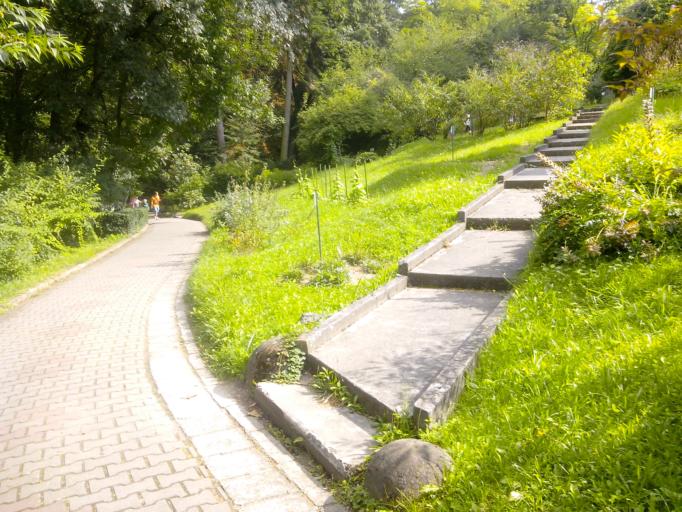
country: RO
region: Cluj
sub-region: Municipiul Cluj-Napoca
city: Cluj-Napoca
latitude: 46.7603
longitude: 23.5863
